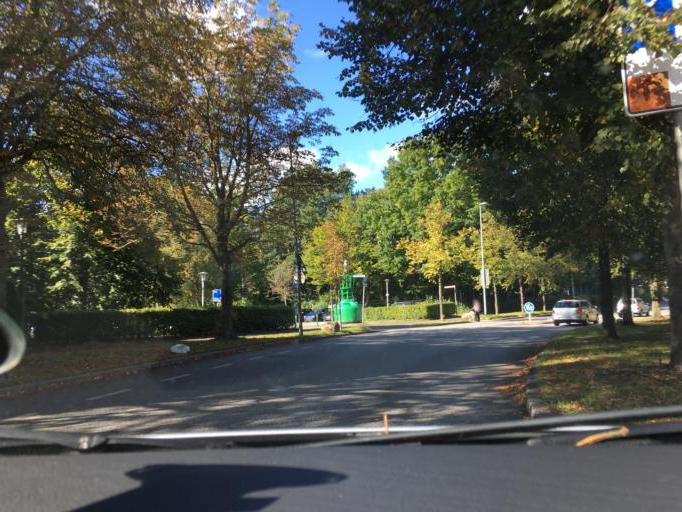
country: DE
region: Schleswig-Holstein
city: Strande
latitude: 54.3956
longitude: 10.1729
